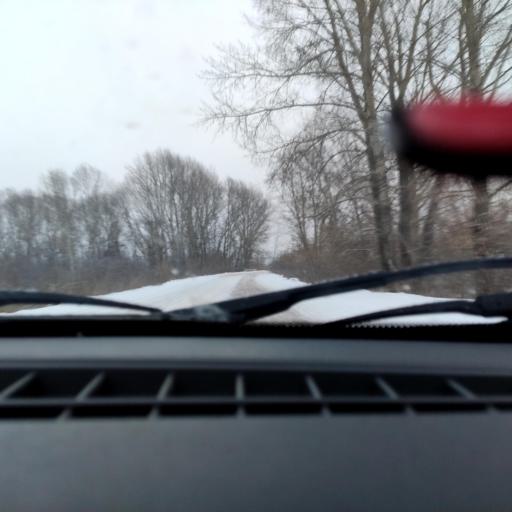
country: RU
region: Bashkortostan
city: Blagoveshchensk
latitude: 54.9110
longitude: 56.0042
